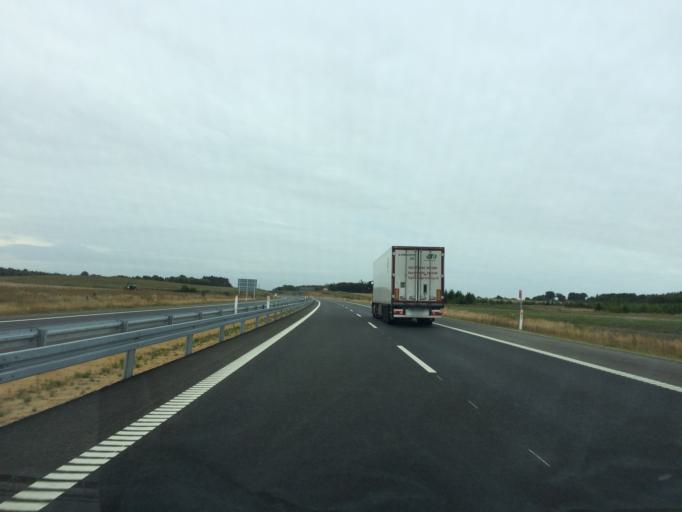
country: DK
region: Central Jutland
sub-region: Herning Kommune
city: Snejbjerg
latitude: 56.1420
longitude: 8.8693
